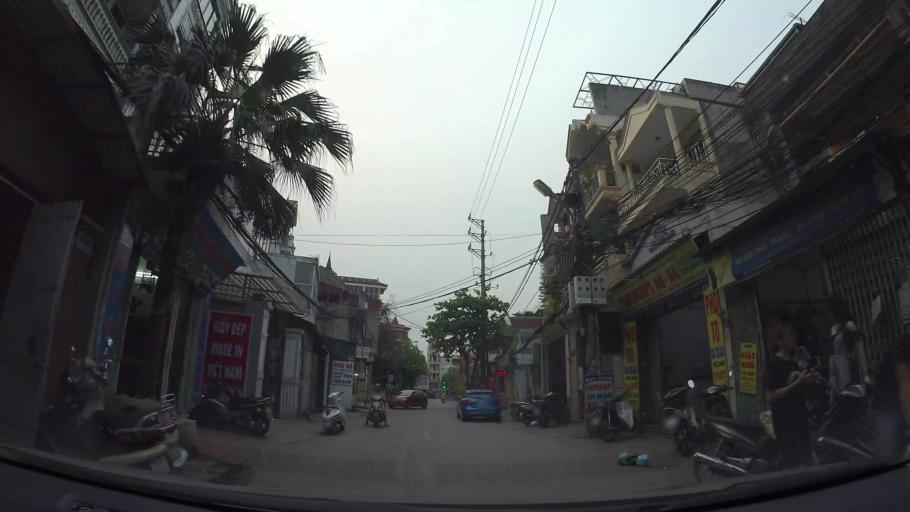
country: VN
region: Ha Noi
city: Hoan Kiem
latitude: 21.0595
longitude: 105.8939
